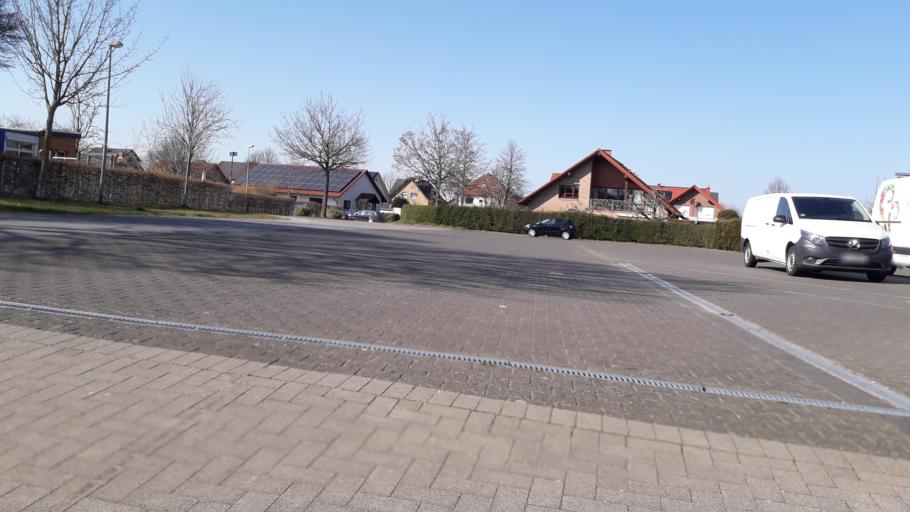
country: DE
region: North Rhine-Westphalia
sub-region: Regierungsbezirk Detmold
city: Paderborn
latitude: 51.6871
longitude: 8.6878
